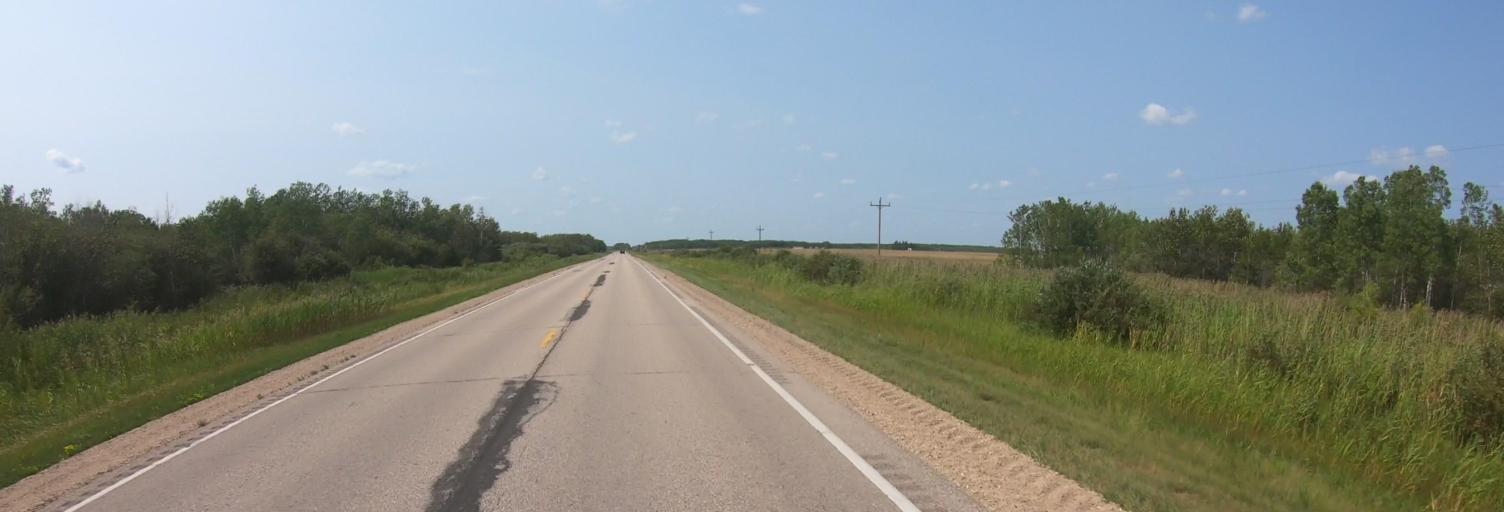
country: US
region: Minnesota
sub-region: Lake of the Woods County
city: Baudette
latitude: 48.7337
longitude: -94.8092
